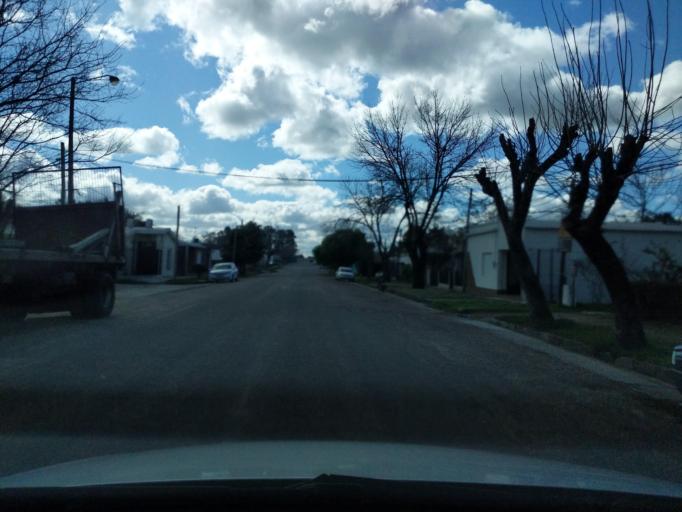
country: UY
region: Florida
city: Florida
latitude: -34.0828
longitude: -56.2211
